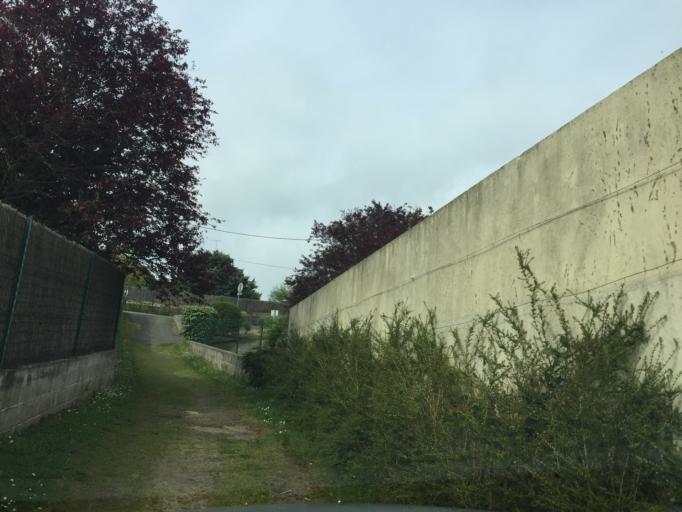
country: FR
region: Brittany
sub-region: Departement des Cotes-d'Armor
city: Saint-Cast-le-Guildo
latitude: 48.6365
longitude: -2.2588
